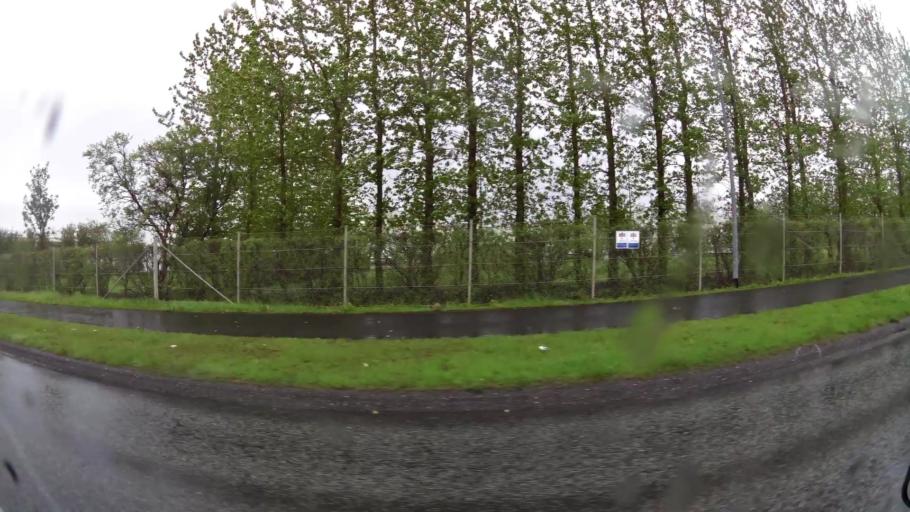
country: IS
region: Capital Region
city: Mosfellsbaer
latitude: 64.1179
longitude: -21.7924
